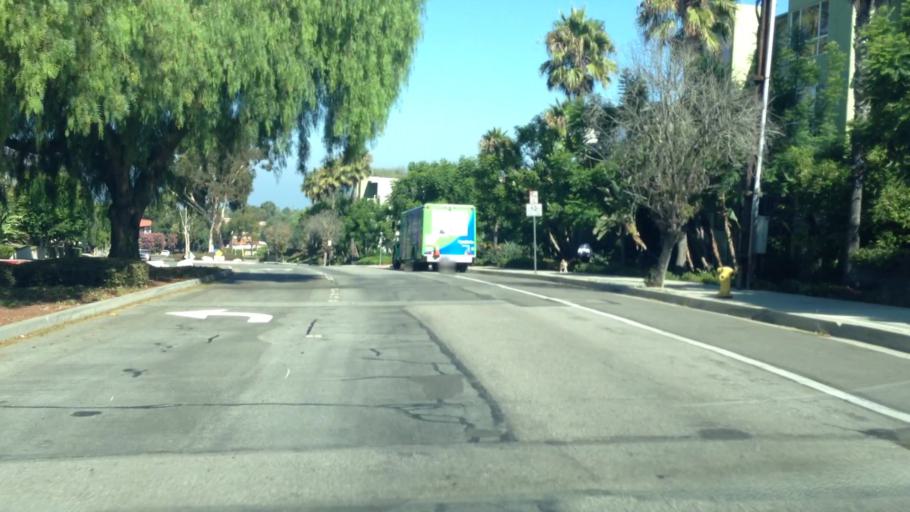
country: US
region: California
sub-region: Los Angeles County
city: Palos Verdes Estates
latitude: 33.7750
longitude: -118.3819
